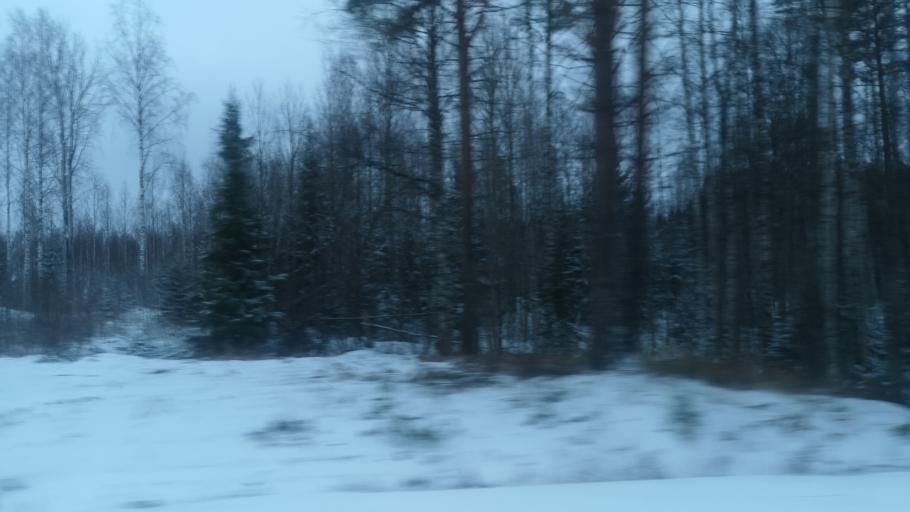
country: FI
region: Southern Savonia
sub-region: Savonlinna
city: Enonkoski
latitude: 62.1081
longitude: 28.6252
